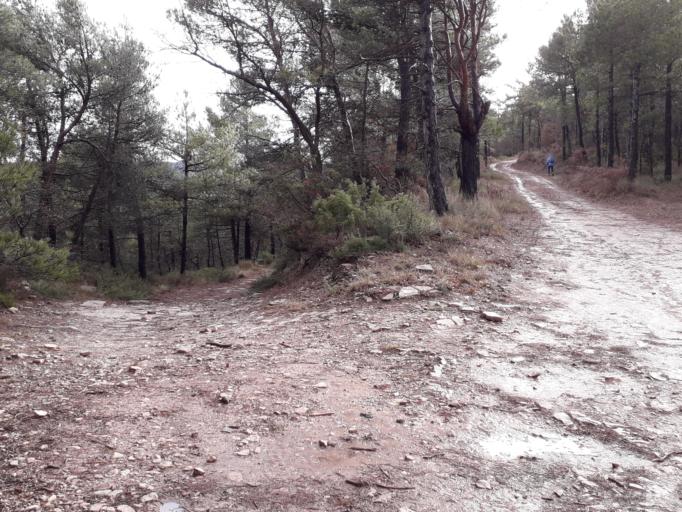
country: ES
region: Catalonia
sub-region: Provincia de Barcelona
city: Bellprat
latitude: 41.5398
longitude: 1.4460
